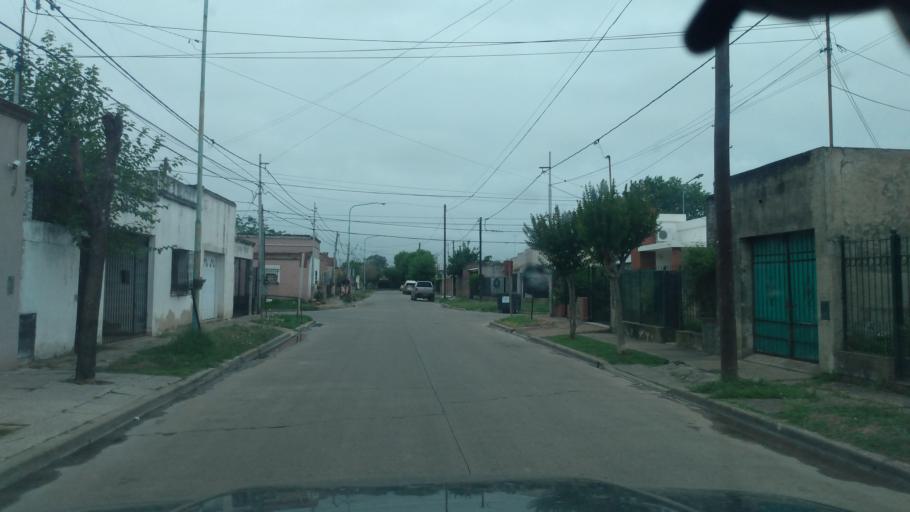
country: AR
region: Buenos Aires
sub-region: Partido de Lujan
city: Lujan
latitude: -34.5754
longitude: -59.1186
